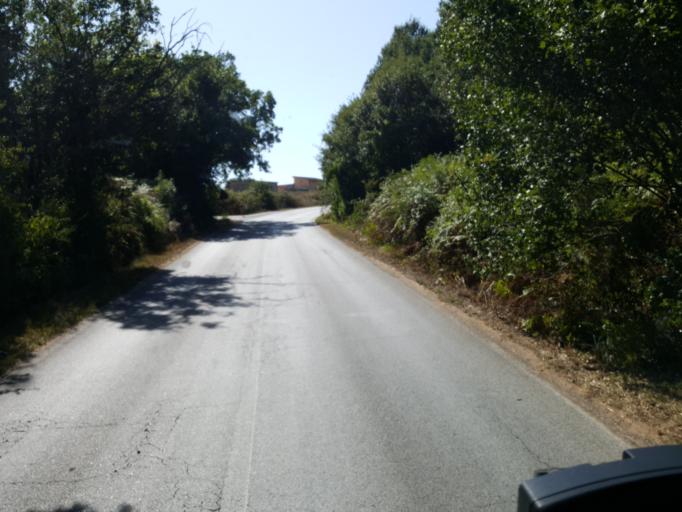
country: IT
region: Latium
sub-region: Citta metropolitana di Roma Capitale
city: Nettuno
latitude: 41.5133
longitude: 12.6472
